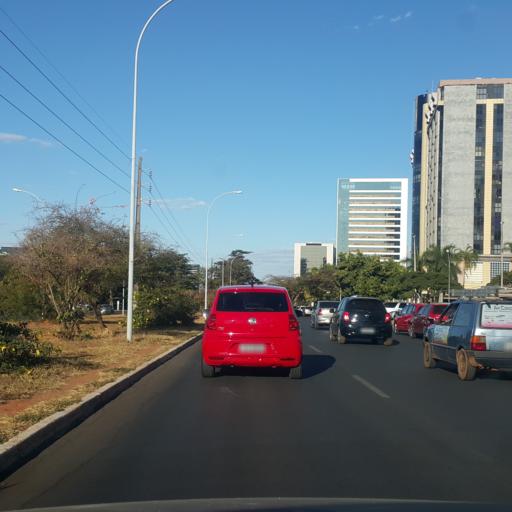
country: BR
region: Federal District
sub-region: Brasilia
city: Brasilia
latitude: -15.7859
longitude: -47.8859
